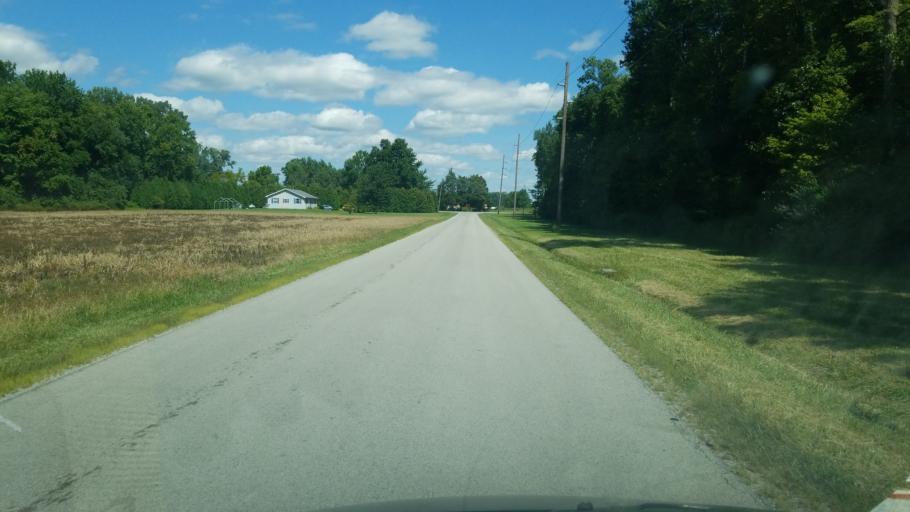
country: US
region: Ohio
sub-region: Lucas County
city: Whitehouse
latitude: 41.4295
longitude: -83.8654
